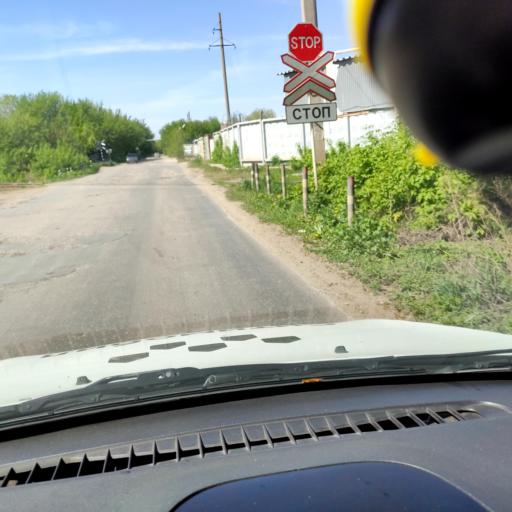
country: RU
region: Samara
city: Tol'yatti
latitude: 53.5680
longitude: 49.2996
